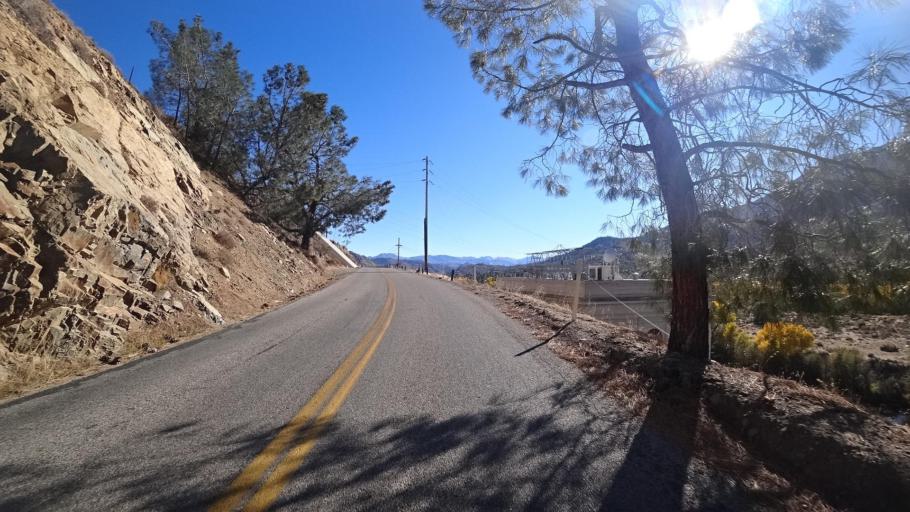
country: US
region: California
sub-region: Kern County
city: Kernville
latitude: 35.7770
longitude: -118.4363
